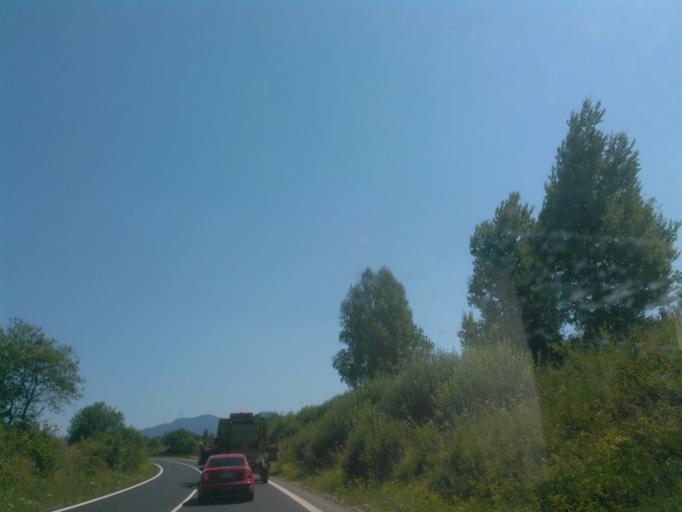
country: SK
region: Zilinsky
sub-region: Okres Liptovsky Mikulas
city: Liptovsky Mikulas
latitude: 49.0556
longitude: 19.4954
